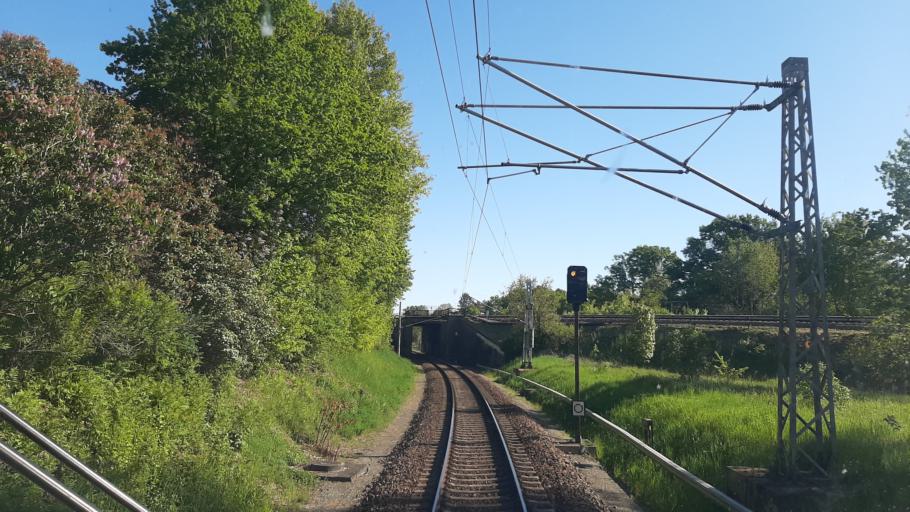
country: DE
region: Brandenburg
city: Birkenwerder
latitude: 52.6780
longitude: 13.2873
